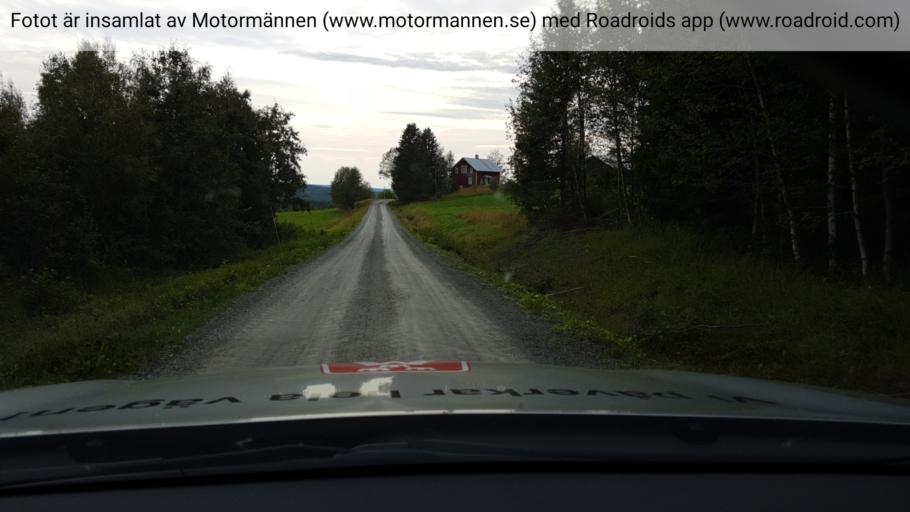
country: SE
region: Jaemtland
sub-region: Krokoms Kommun
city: Valla
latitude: 63.5734
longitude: 13.9340
